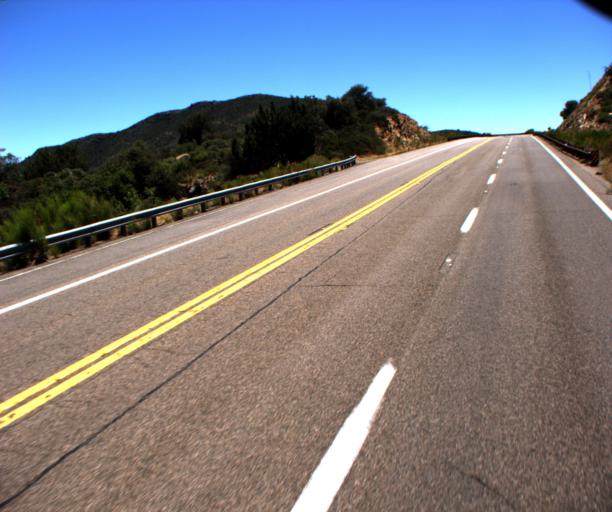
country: US
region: Arizona
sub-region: Gila County
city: Globe
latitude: 33.2708
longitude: -110.7636
